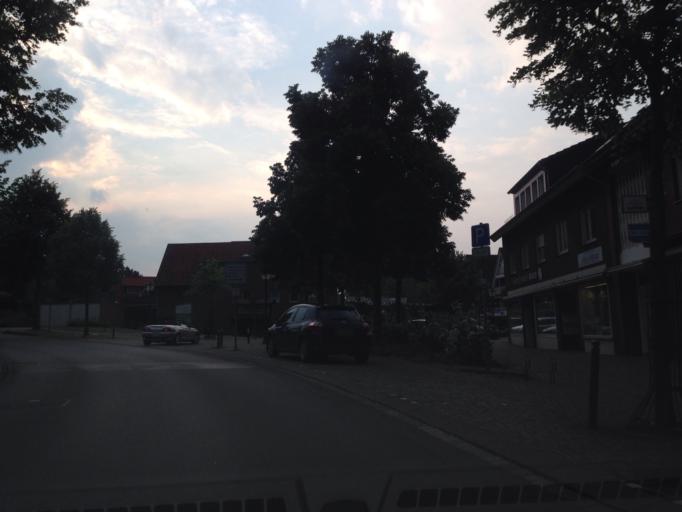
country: DE
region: North Rhine-Westphalia
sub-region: Regierungsbezirk Munster
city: Havixbeck
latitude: 51.9742
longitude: 7.4132
